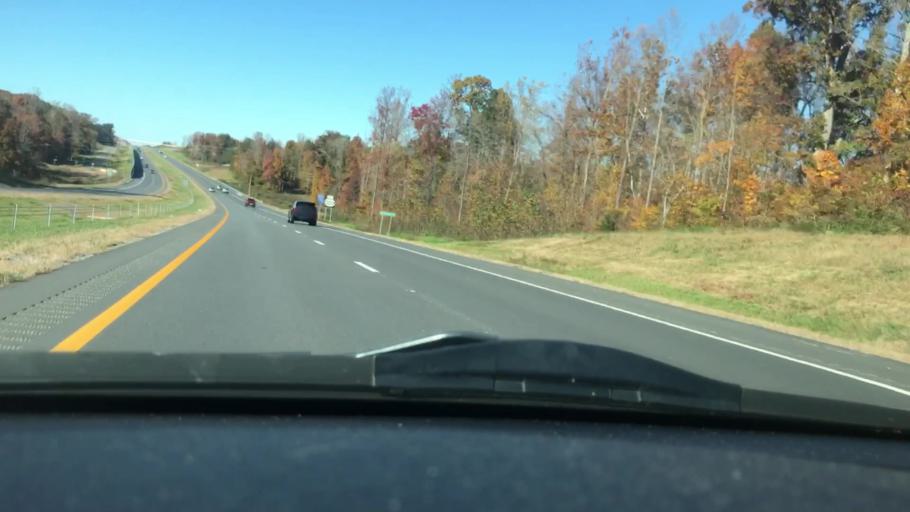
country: US
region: North Carolina
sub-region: Guilford County
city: Summerfield
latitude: 36.2536
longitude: -79.9229
